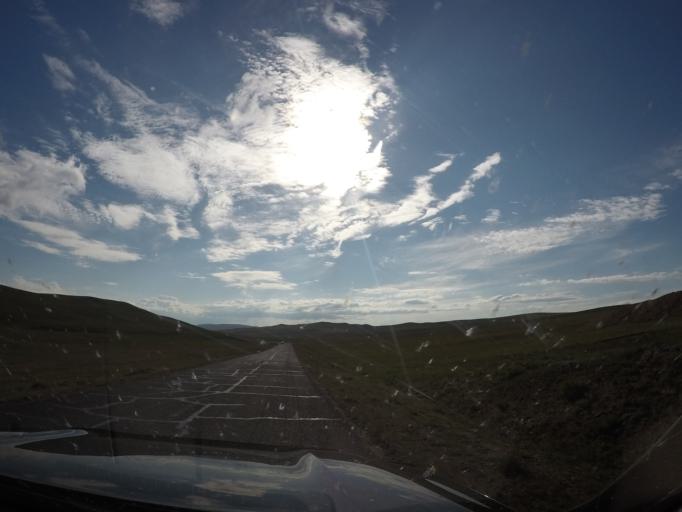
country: MN
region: Hentiy
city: Modot
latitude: 47.7965
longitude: 108.6920
